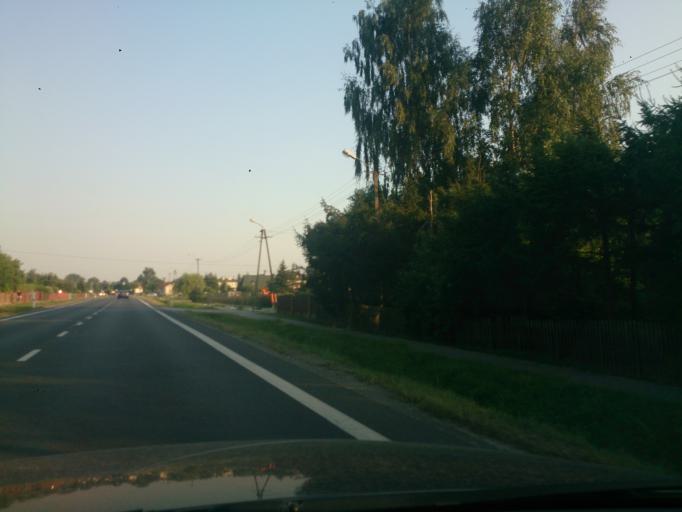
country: PL
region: Subcarpathian Voivodeship
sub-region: Powiat kolbuszowski
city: Kolbuszowa
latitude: 50.2294
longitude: 21.7905
